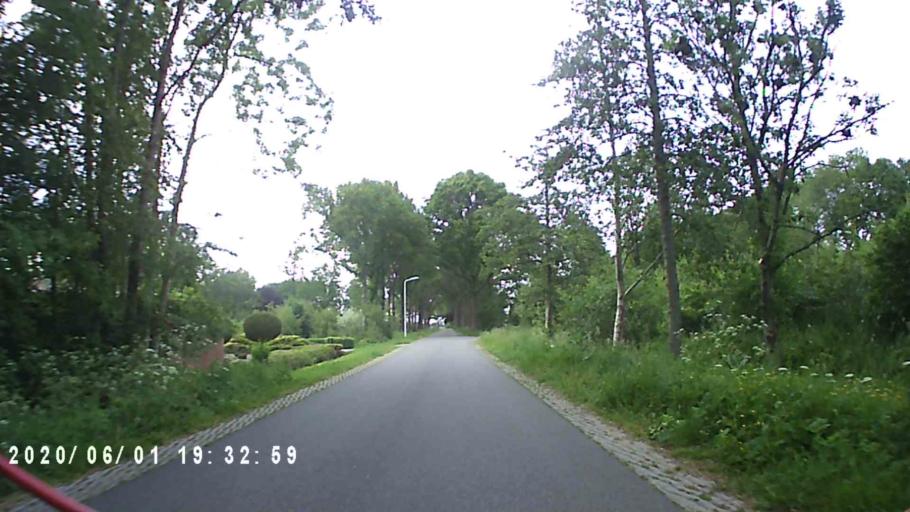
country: NL
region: Friesland
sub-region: Gemeente Achtkarspelen
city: Augustinusga
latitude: 53.2129
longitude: 6.1572
